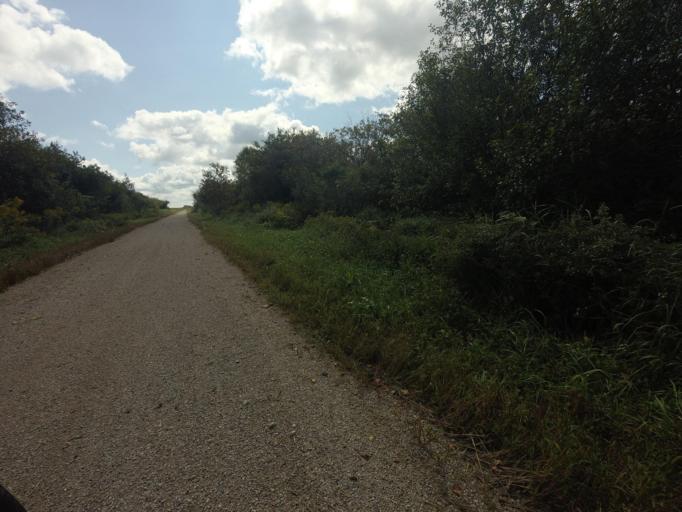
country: CA
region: Ontario
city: Huron East
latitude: 43.6463
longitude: -81.2172
